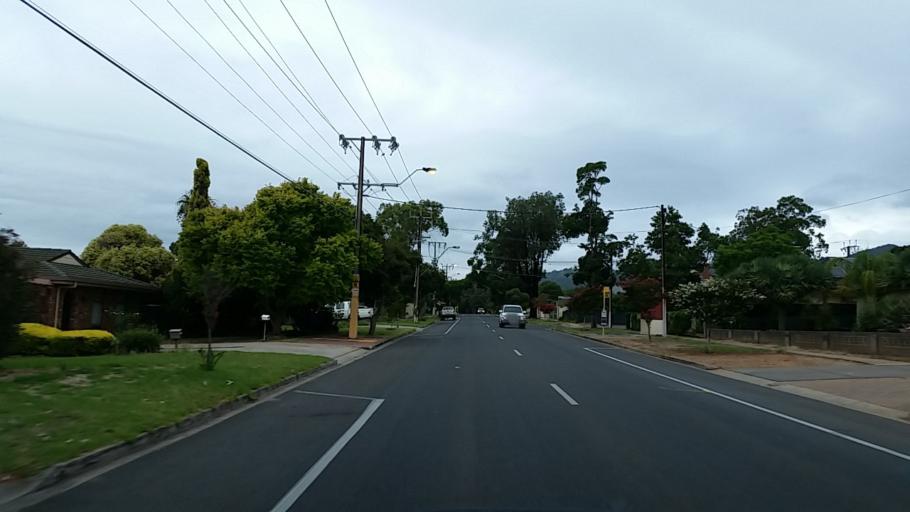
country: AU
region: South Australia
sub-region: Campbelltown
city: Athelstone
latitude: -34.8689
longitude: 138.6864
